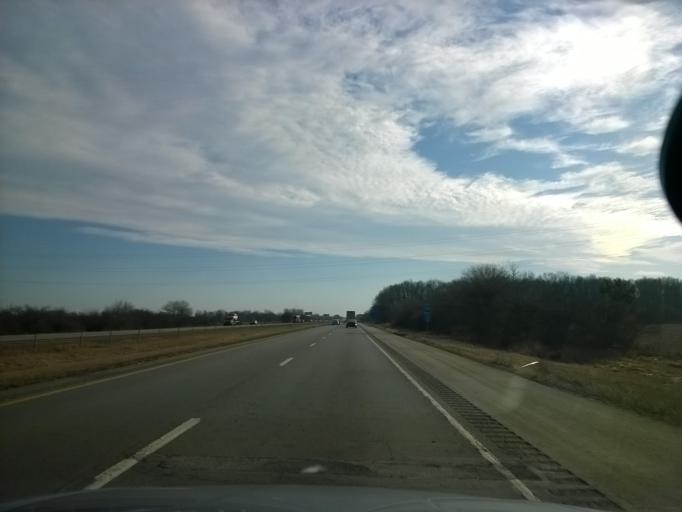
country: US
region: Indiana
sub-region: Johnson County
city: Franklin
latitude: 39.5145
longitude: -86.0229
